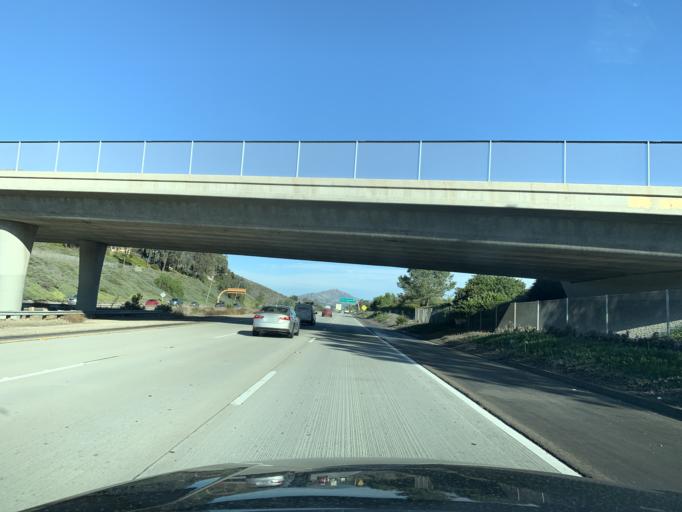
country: US
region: California
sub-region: San Diego County
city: Fairbanks Ranch
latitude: 32.9556
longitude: -117.1217
